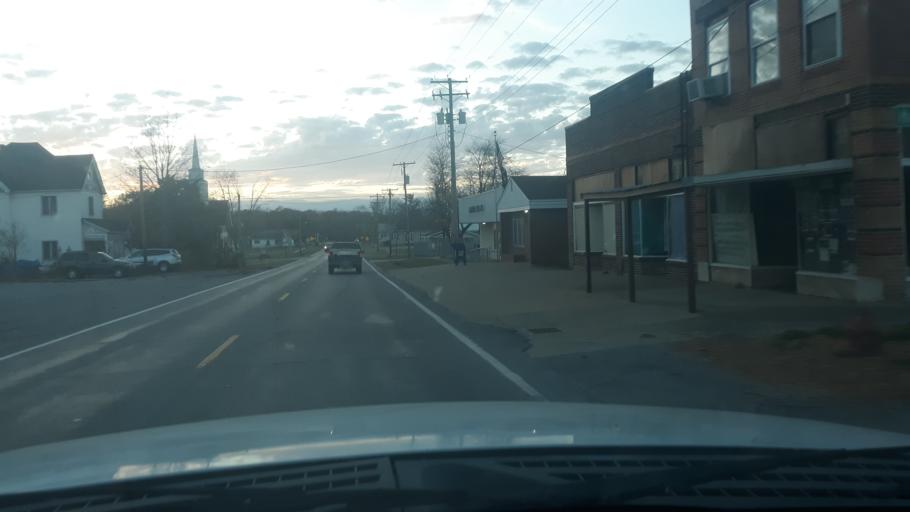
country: US
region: Illinois
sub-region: Saline County
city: Harrisburg
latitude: 37.8407
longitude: -88.6120
